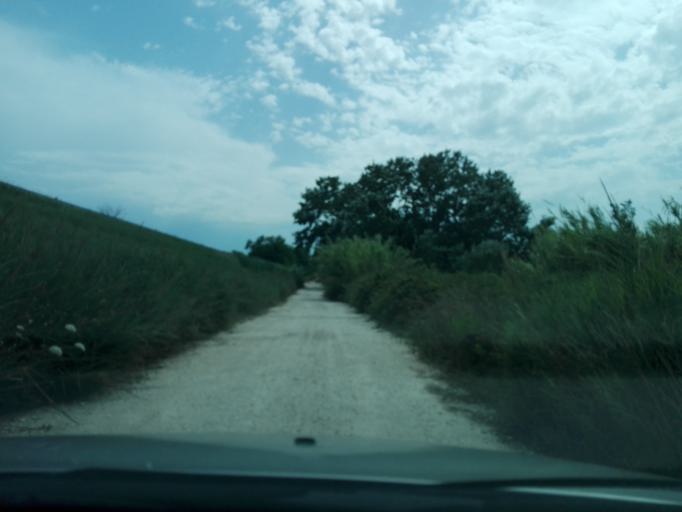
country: IT
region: Abruzzo
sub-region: Provincia di Pescara
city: Cappelle sul Tavo
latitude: 42.4895
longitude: 14.1117
